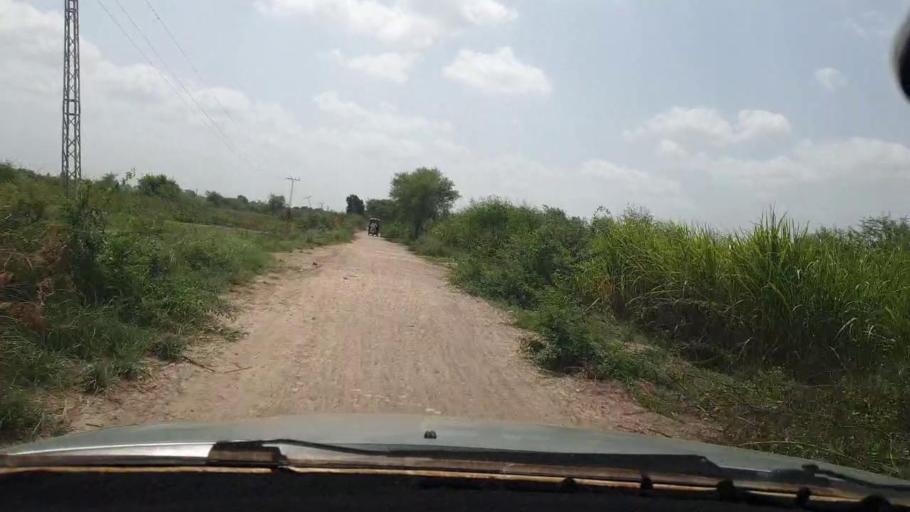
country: PK
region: Sindh
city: Tando Bago
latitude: 24.7544
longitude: 69.1702
